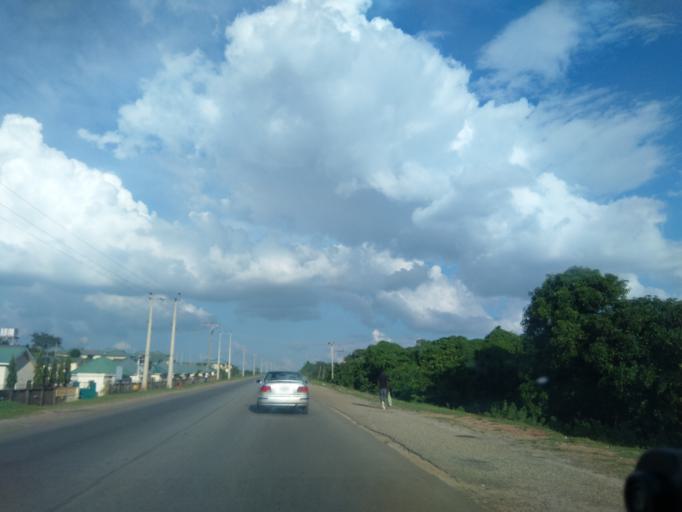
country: NG
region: Abuja Federal Capital Territory
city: Abuja
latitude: 9.0414
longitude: 7.3946
